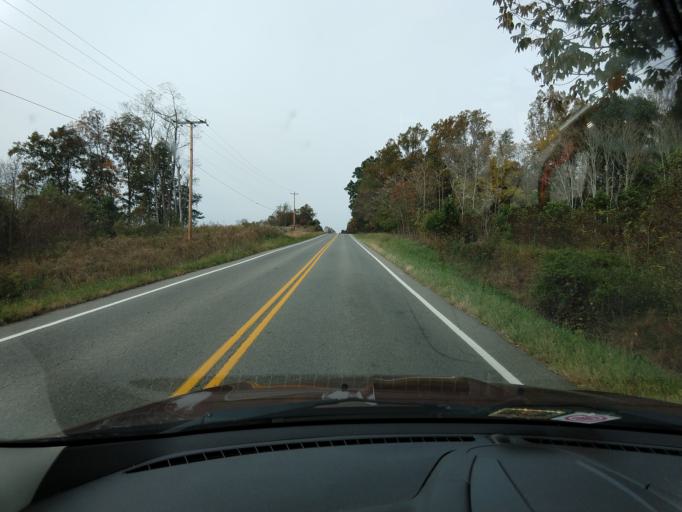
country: US
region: Virginia
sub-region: Franklin County
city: Union Hall
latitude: 36.9898
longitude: -79.6647
